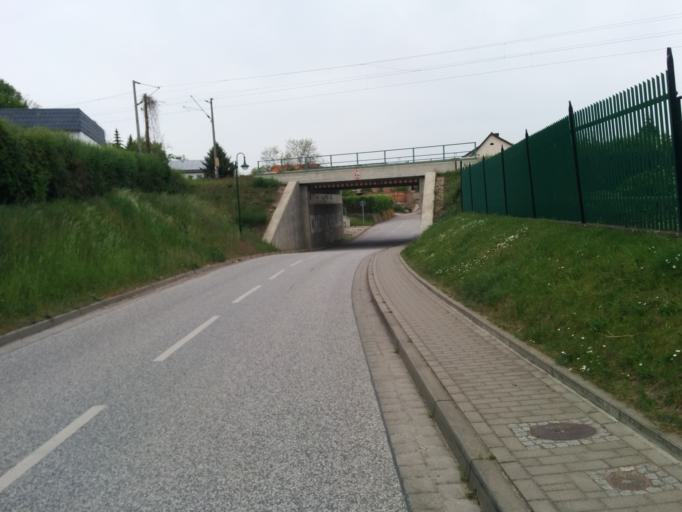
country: DE
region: Saxony-Anhalt
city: Zscherben
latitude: 51.4645
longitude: 11.8714
